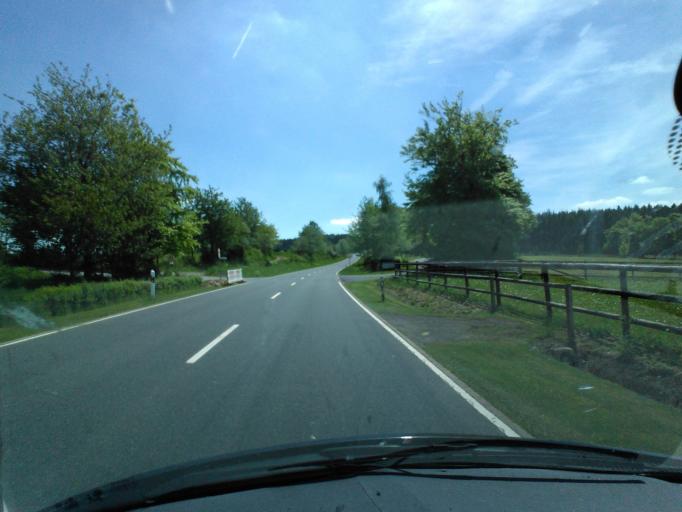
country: DE
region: Rheinland-Pfalz
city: Winterspelt
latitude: 50.2105
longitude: 6.2234
